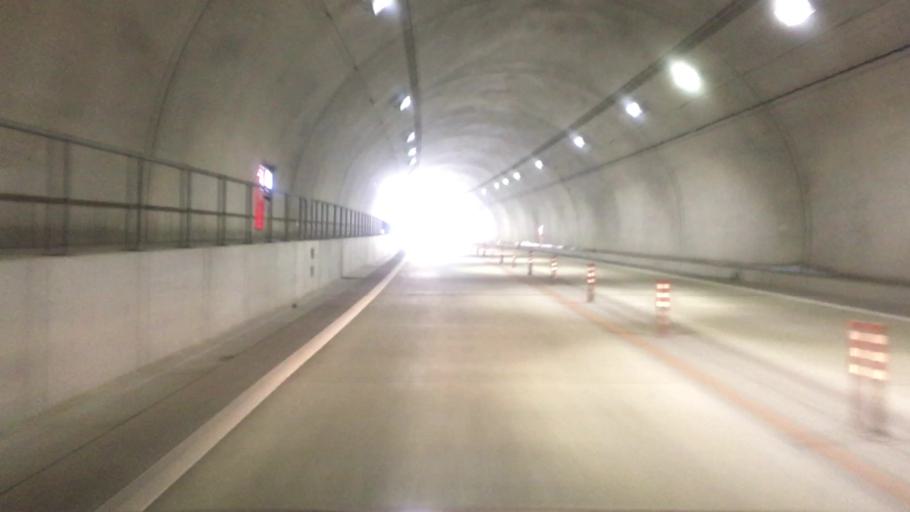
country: JP
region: Hyogo
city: Toyooka
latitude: 35.6386
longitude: 134.5638
